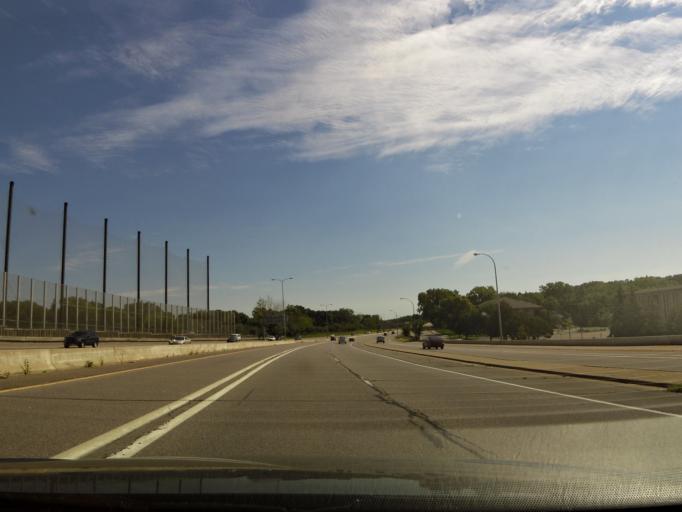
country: US
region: Minnesota
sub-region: Hennepin County
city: Saint Louis Park
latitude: 44.9739
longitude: -93.3893
